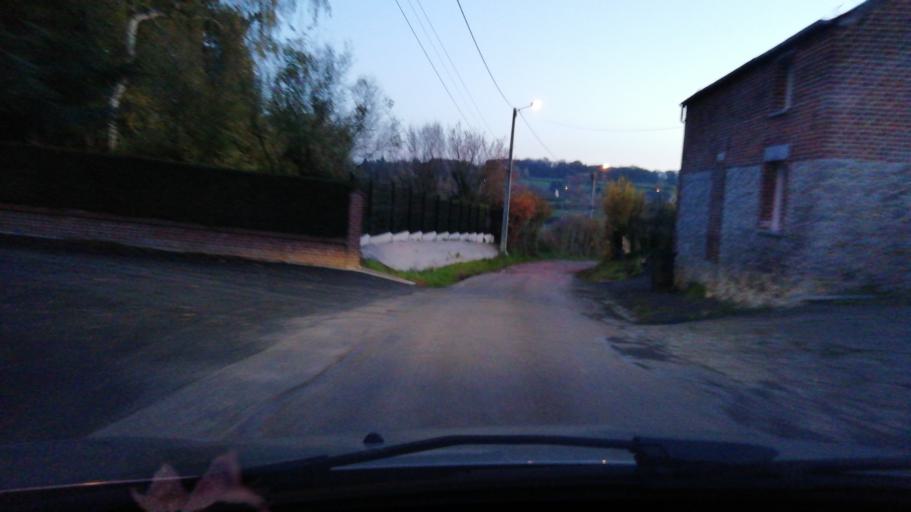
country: FR
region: Nord-Pas-de-Calais
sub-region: Departement du Nord
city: Marpent
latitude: 50.2577
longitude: 4.0879
